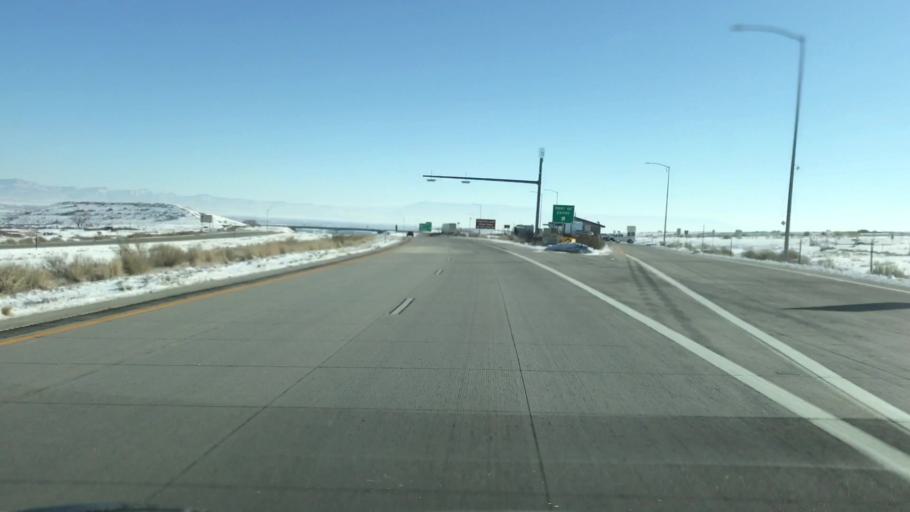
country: US
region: Colorado
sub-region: Mesa County
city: Loma
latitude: 39.1787
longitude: -108.8220
